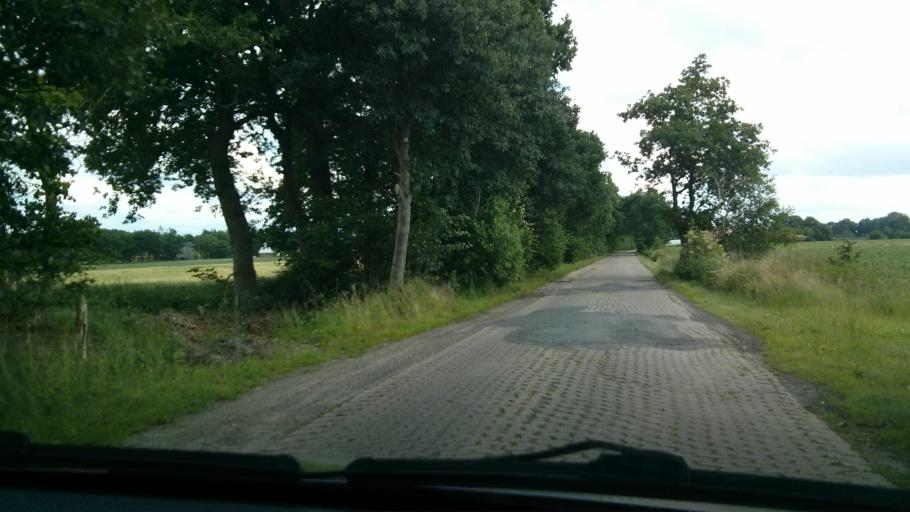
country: DE
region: Lower Saxony
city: Loxstedt
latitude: 53.4970
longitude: 8.6865
